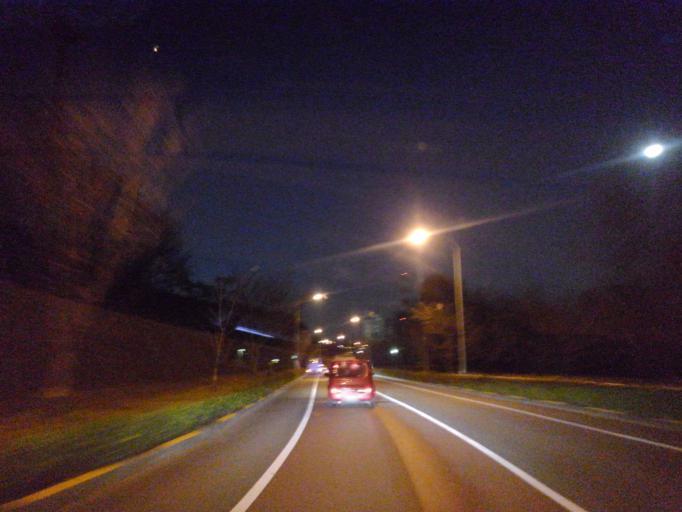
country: JP
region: Tokyo
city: Kokubunji
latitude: 35.6273
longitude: 139.4736
